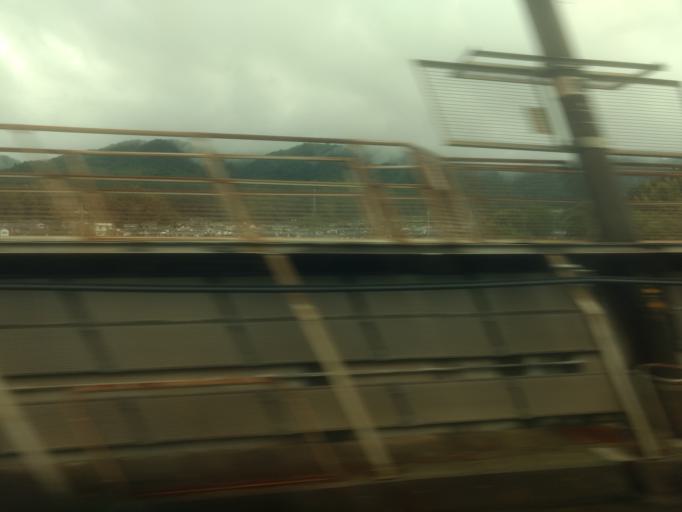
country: JP
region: Yamaguchi
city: Kudamatsu
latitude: 34.0354
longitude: 131.8887
